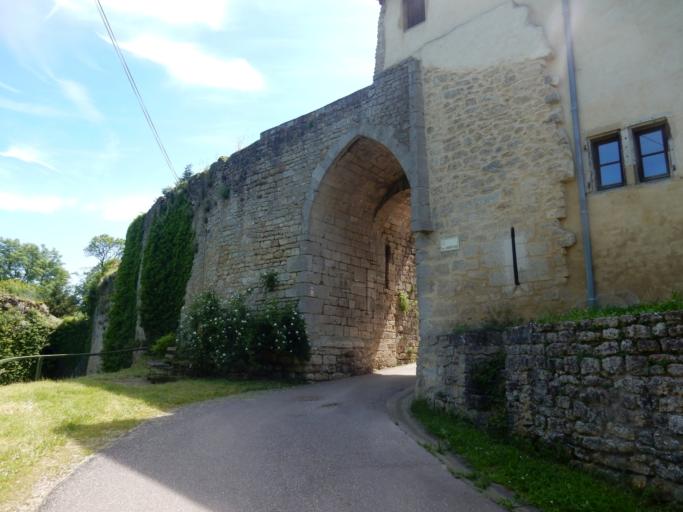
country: FR
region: Lorraine
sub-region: Departement de Meurthe-et-Moselle
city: Pagny-sur-Moselle
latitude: 48.9796
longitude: 5.9946
